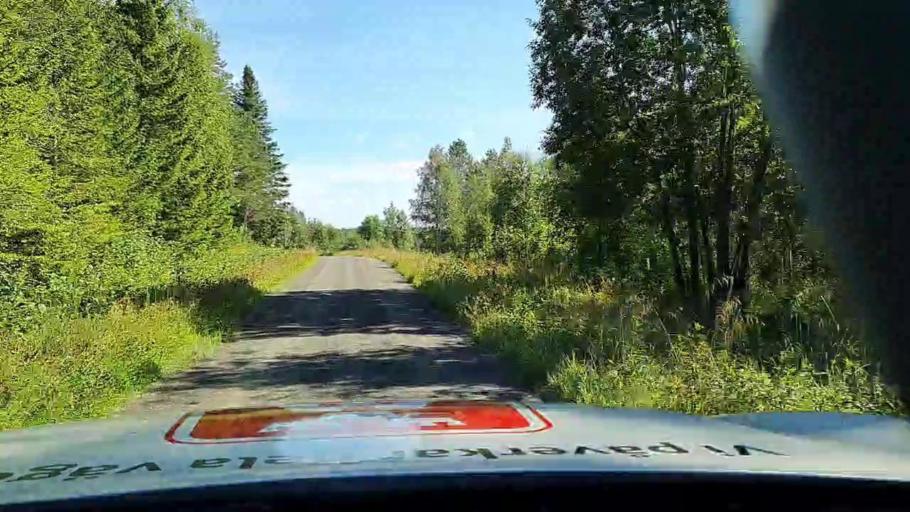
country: SE
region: Jaemtland
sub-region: Krokoms Kommun
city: Krokom
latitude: 63.7727
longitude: 14.6394
